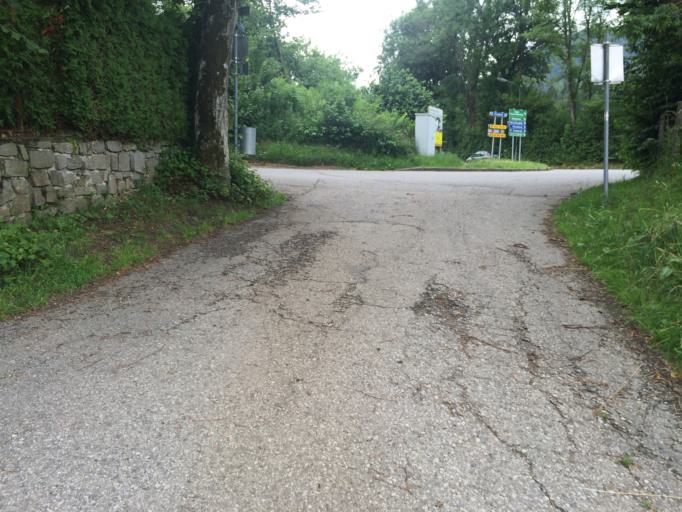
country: AT
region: Carinthia
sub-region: Villach Stadt
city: Villach
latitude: 46.5957
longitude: 13.8266
